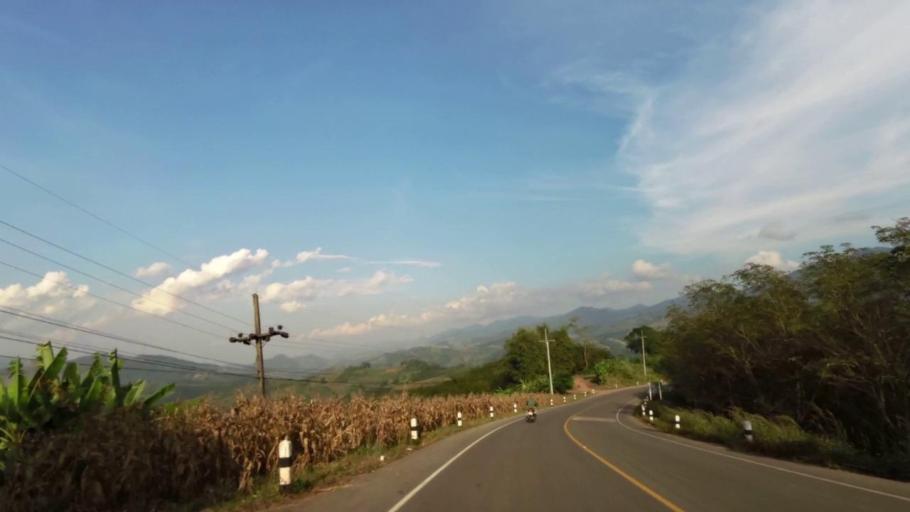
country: TH
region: Chiang Rai
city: Khun Tan
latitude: 19.8538
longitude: 100.3818
